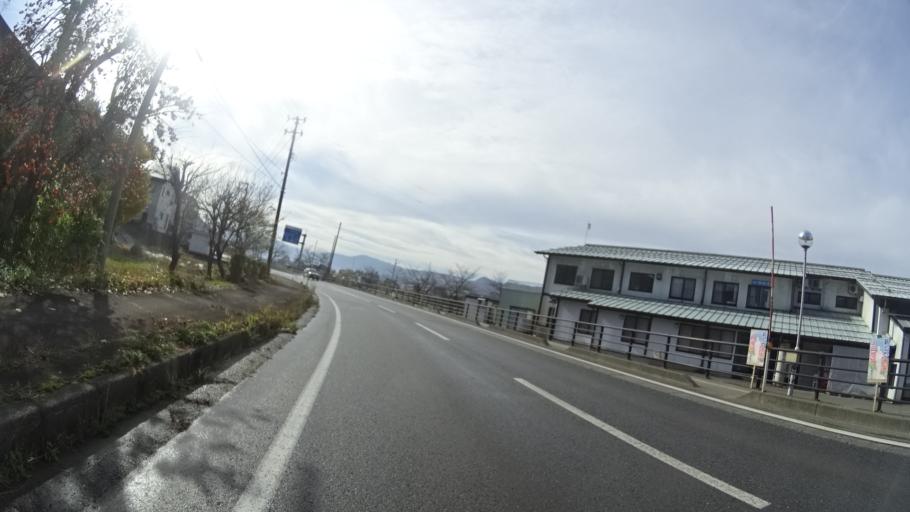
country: JP
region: Niigata
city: Muikamachi
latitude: 37.0838
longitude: 138.8992
